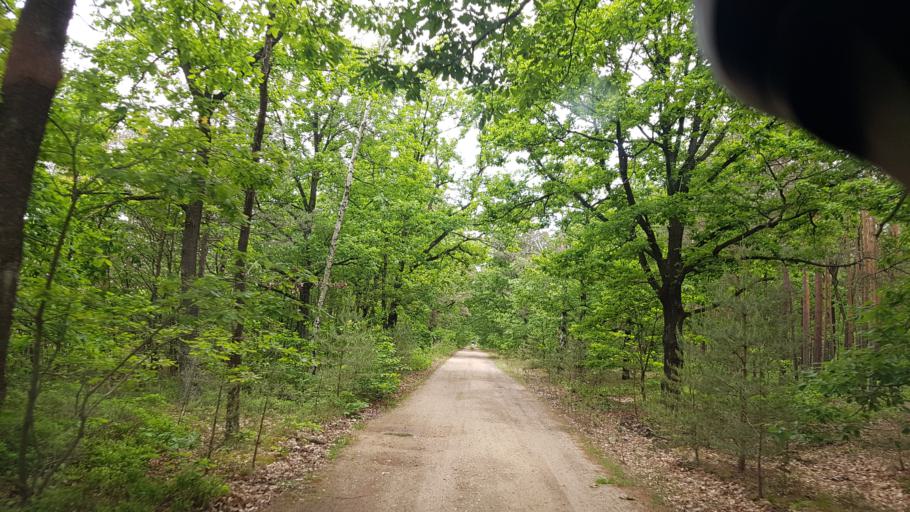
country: DE
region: Brandenburg
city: Hohenleipisch
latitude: 51.5183
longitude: 13.5157
